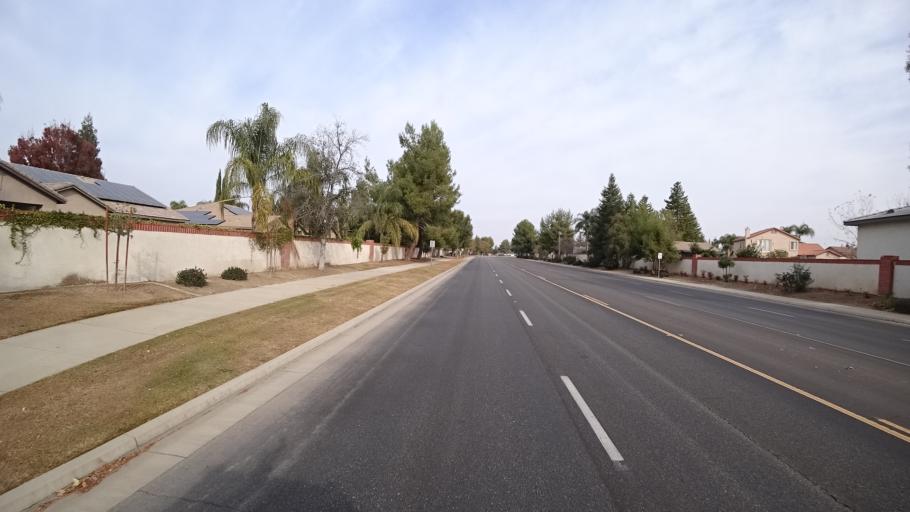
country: US
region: California
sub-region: Kern County
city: Rosedale
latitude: 35.3454
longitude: -119.1347
